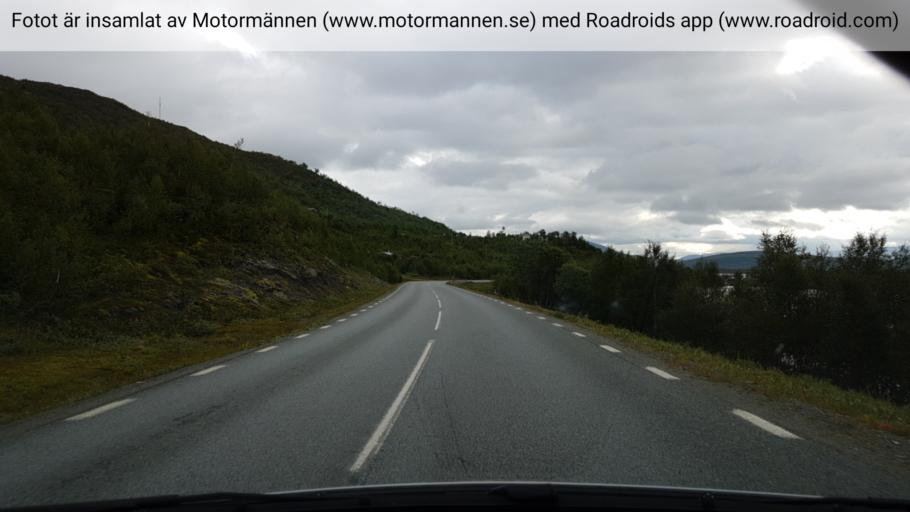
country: NO
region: Nordland
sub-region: Rana
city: Mo i Rana
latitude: 66.1267
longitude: 14.6552
